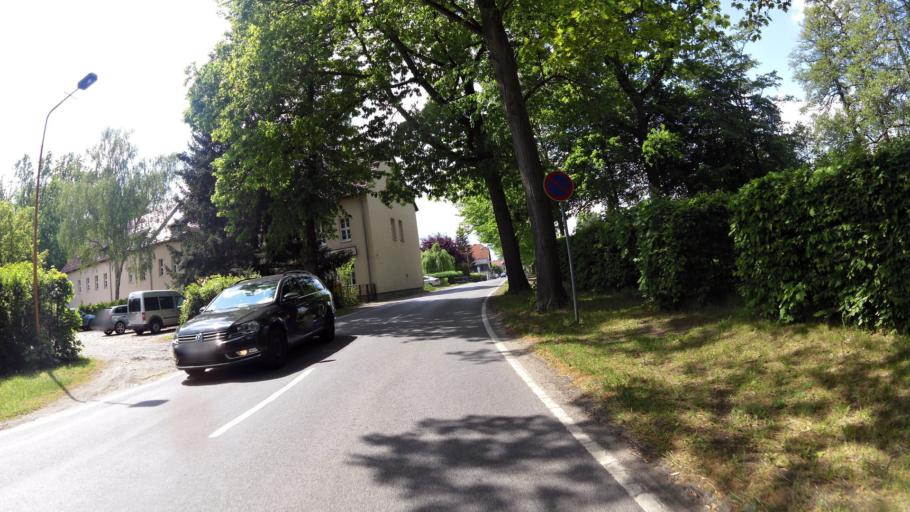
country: DE
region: Brandenburg
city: Gross Koris
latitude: 52.1692
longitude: 13.6963
